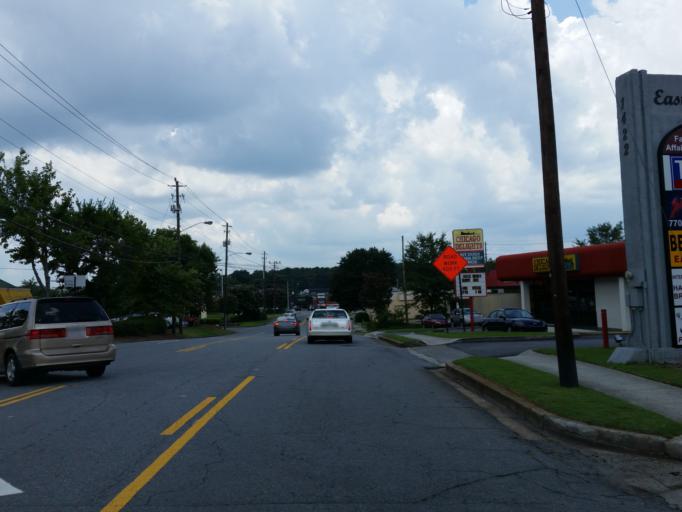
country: US
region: Georgia
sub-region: Cobb County
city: Marietta
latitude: 33.9499
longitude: -84.5113
